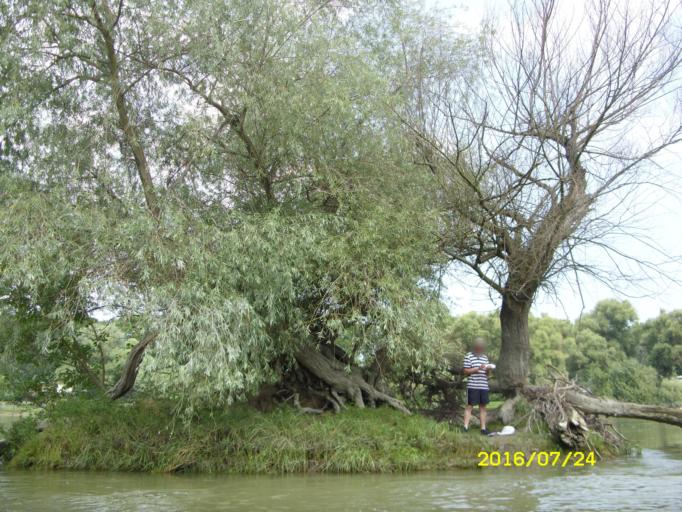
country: HU
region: Pest
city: Budakalasz
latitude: 47.6141
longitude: 19.0866
